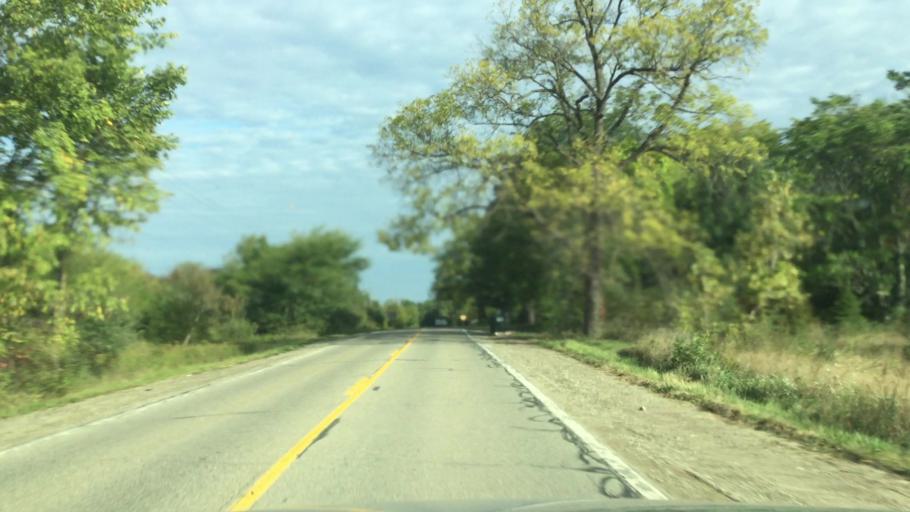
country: US
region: Michigan
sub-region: Livingston County
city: Howell
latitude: 42.5880
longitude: -83.8998
